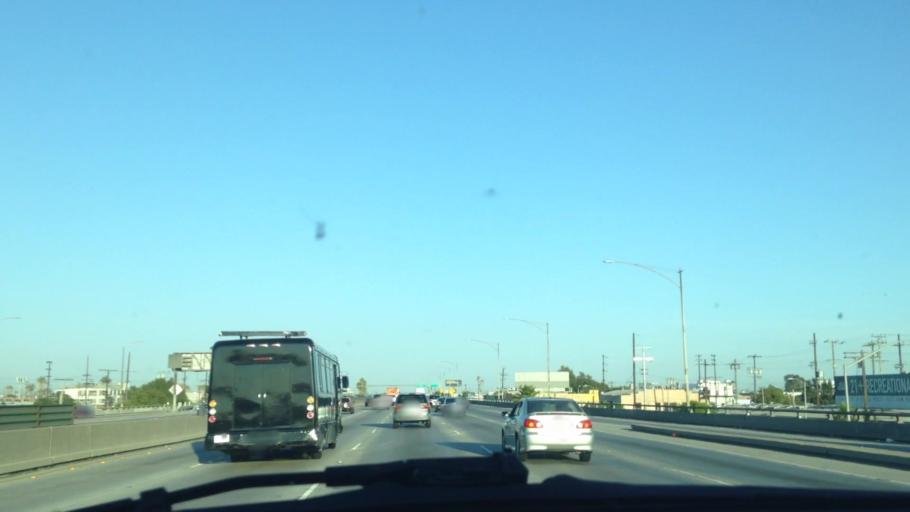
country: US
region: California
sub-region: Los Angeles County
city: Los Angeles
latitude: 34.0281
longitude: -118.2538
